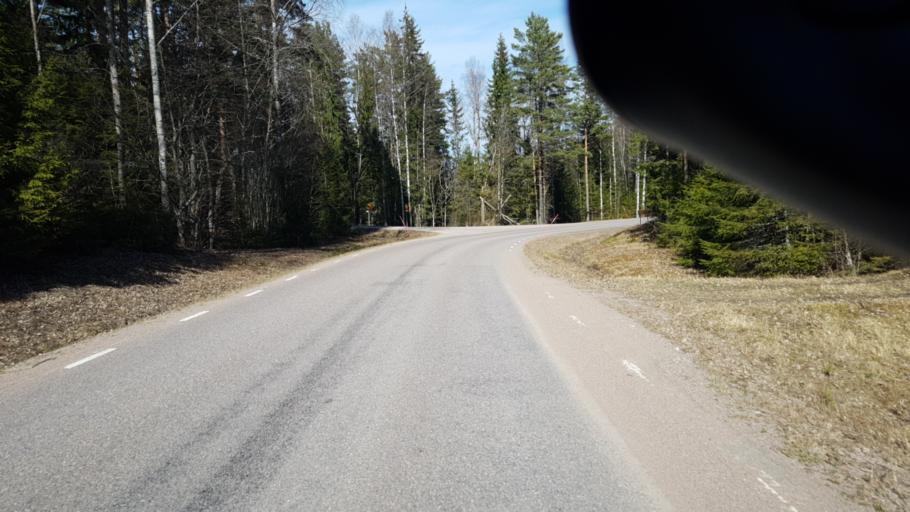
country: SE
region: Vaermland
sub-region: Arvika Kommun
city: Arvika
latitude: 59.6057
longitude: 12.7605
